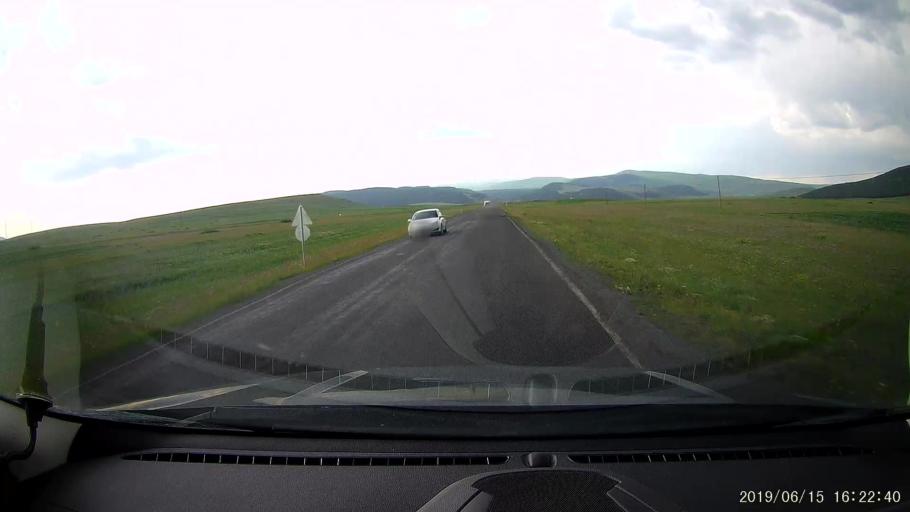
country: TR
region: Ardahan
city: Hanak
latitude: 41.1859
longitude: 42.8532
